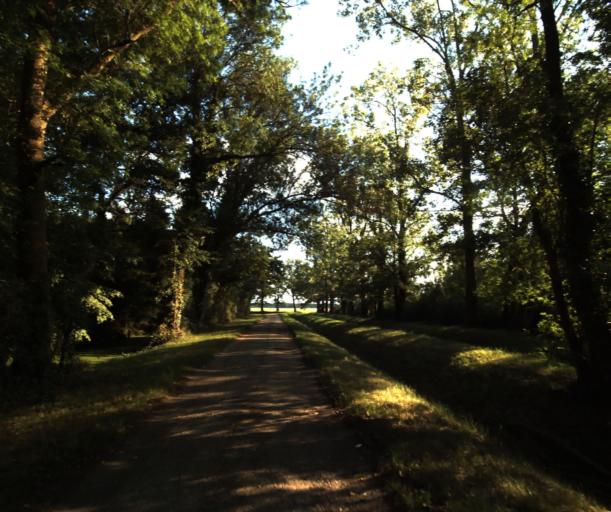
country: FR
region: Midi-Pyrenees
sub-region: Departement de la Haute-Garonne
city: Labastidette
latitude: 43.4793
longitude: 1.2416
